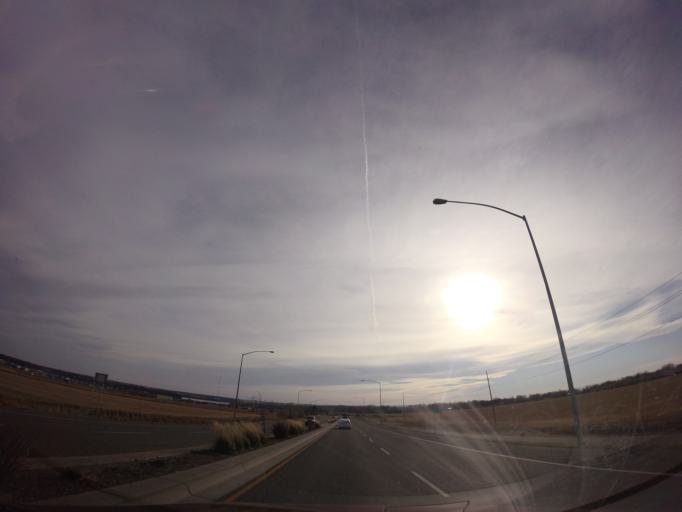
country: US
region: Montana
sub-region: Yellowstone County
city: Billings
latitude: 45.7386
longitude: -108.6175
